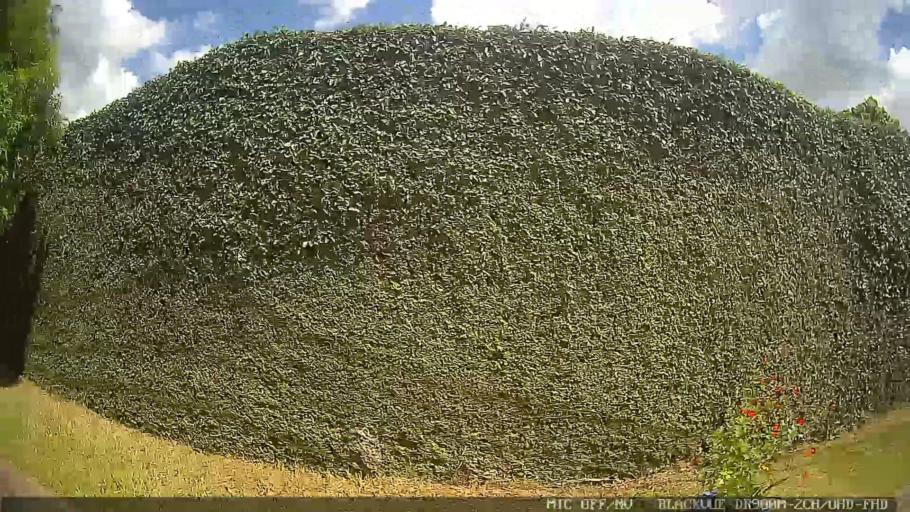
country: BR
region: Sao Paulo
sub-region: Atibaia
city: Atibaia
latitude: -23.1449
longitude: -46.5615
